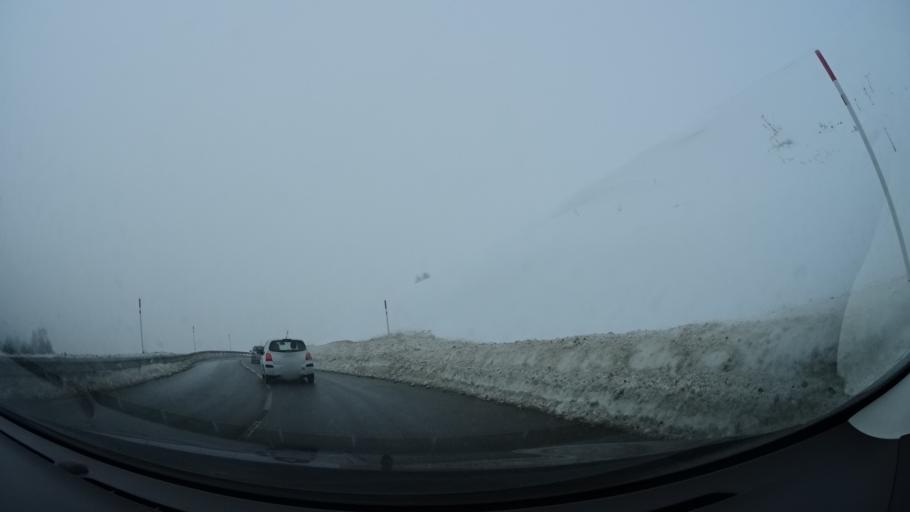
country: AD
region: Encamp
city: Pas de la Casa
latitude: 42.5568
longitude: 1.7688
